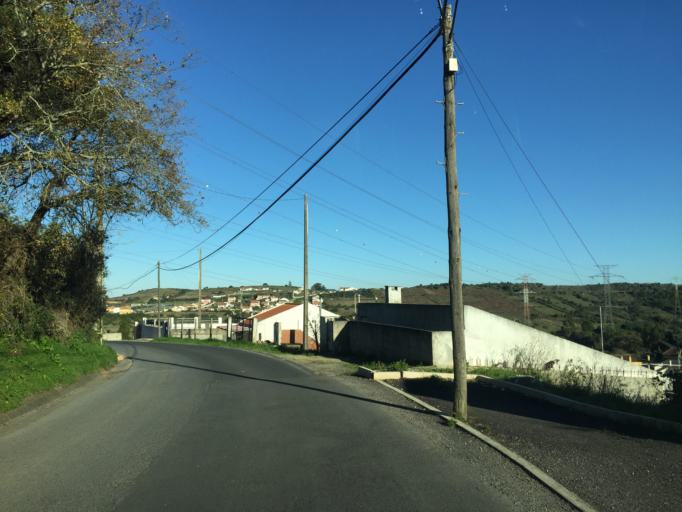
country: PT
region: Lisbon
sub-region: Odivelas
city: Canecas
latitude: 38.8223
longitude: -9.2348
